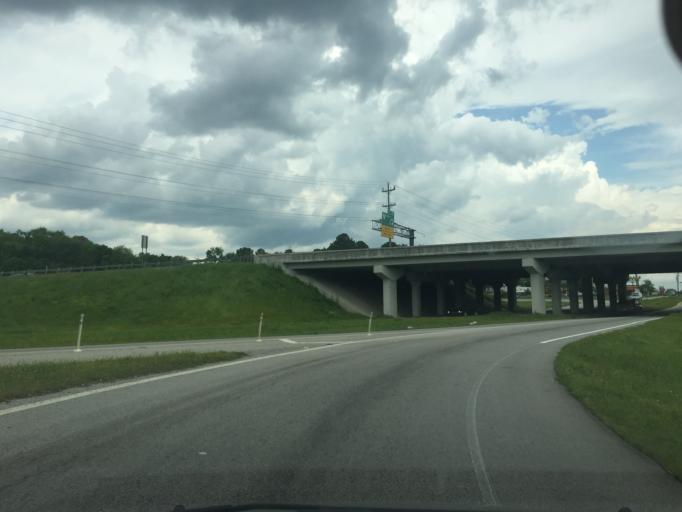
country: US
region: Tennessee
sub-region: Hamilton County
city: East Chattanooga
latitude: 35.0820
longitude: -85.2072
